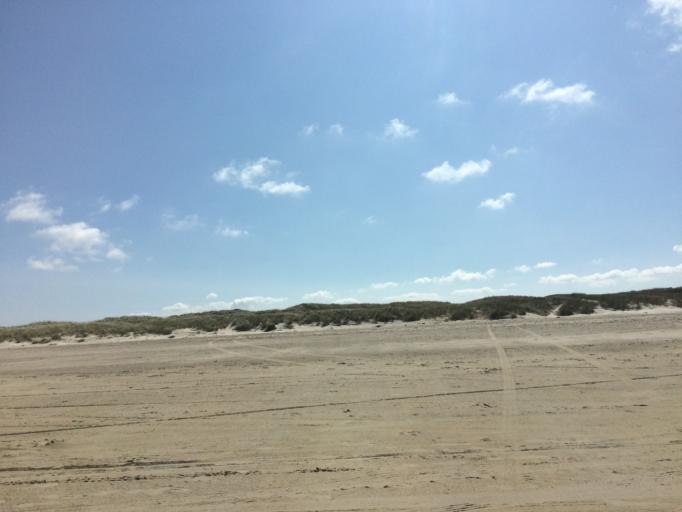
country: DK
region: North Denmark
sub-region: Jammerbugt Kommune
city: Brovst
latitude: 57.2211
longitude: 9.5323
